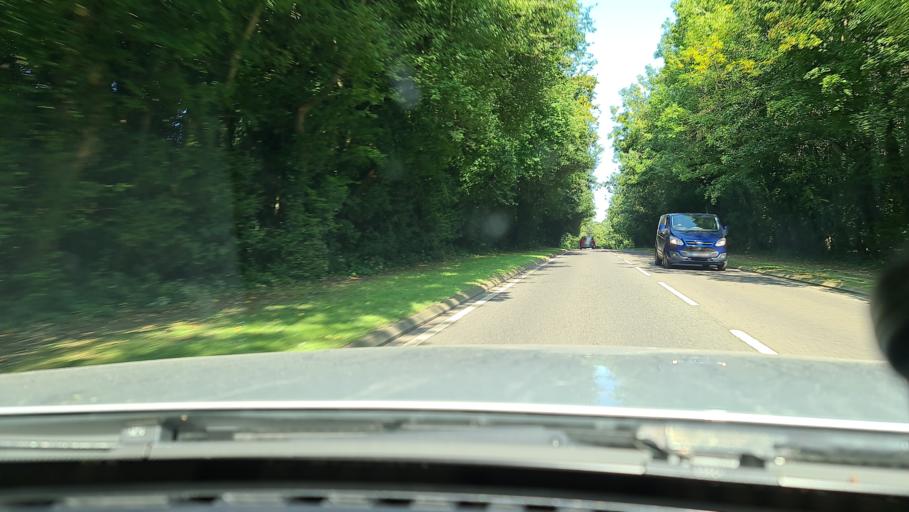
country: GB
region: England
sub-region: Northamptonshire
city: Daventry
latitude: 52.2652
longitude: -1.1578
